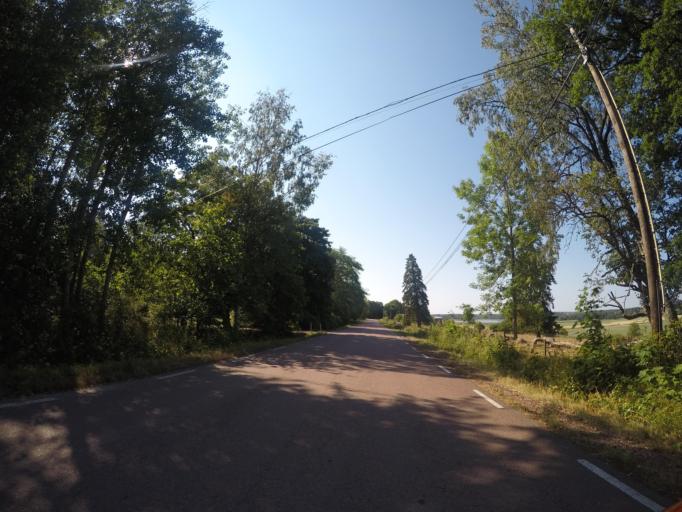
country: AX
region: Alands landsbygd
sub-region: Jomala
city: Jomala
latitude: 60.2103
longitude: 19.9735
